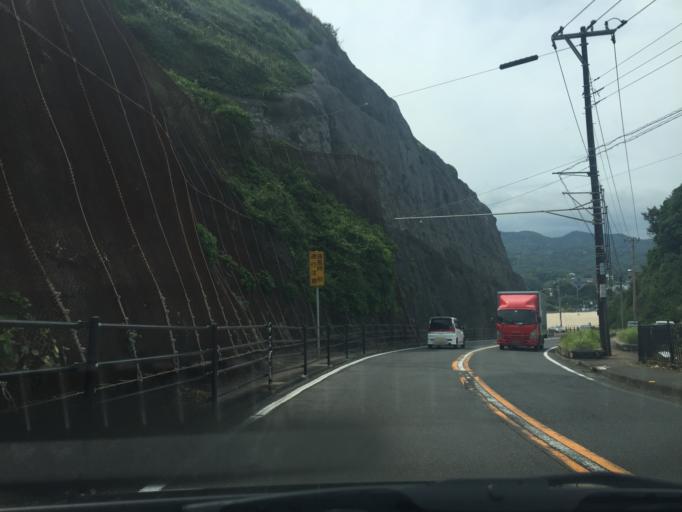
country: JP
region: Shizuoka
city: Shimoda
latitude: 34.6857
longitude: 138.9744
